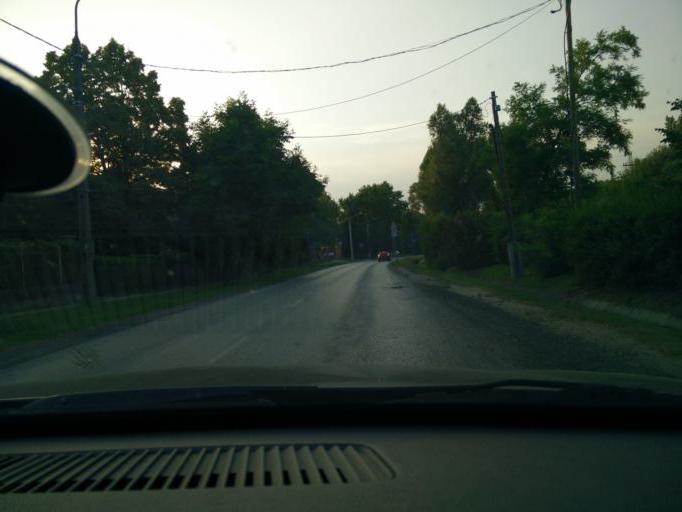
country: HU
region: Pest
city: Toeroekbalint
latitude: 47.4430
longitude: 18.9117
